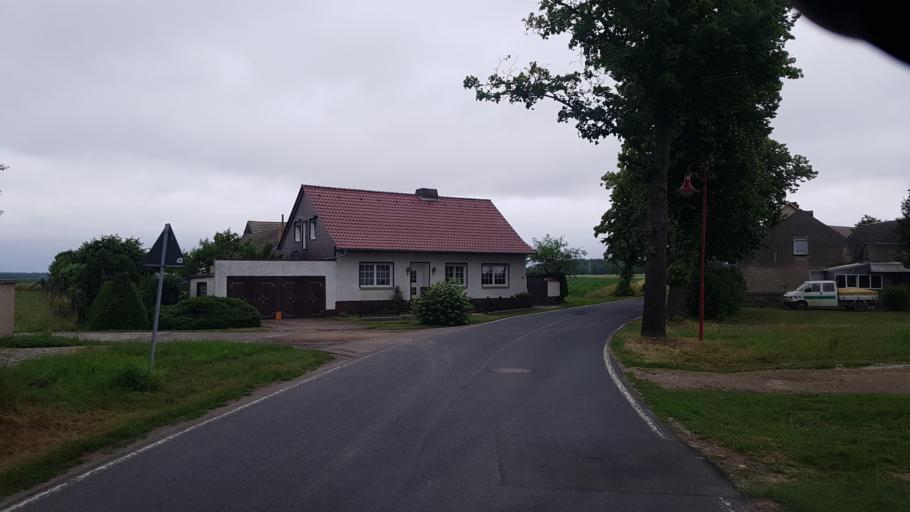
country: DE
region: Brandenburg
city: Ihlow
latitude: 51.9350
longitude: 13.2116
